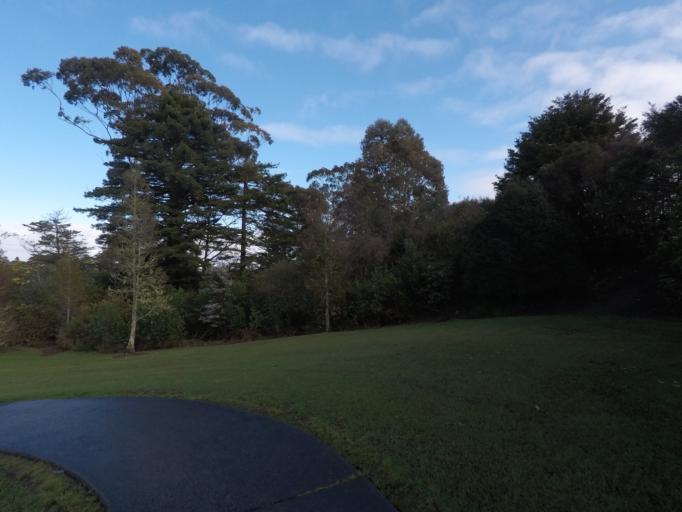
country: NZ
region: Auckland
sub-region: Auckland
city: Warkworth
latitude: -36.4241
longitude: 174.7243
